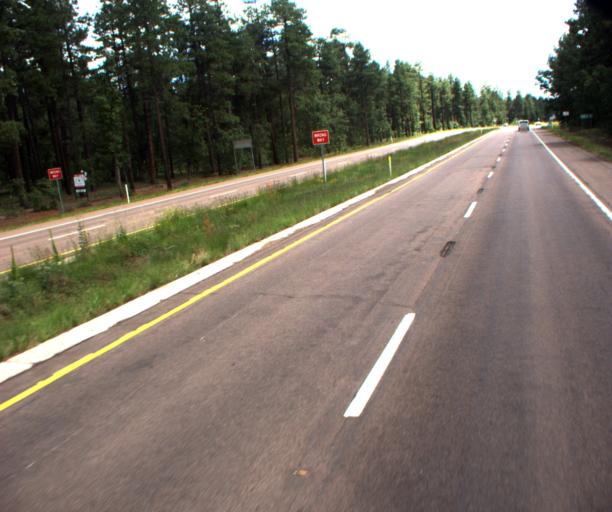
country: US
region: Arizona
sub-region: Navajo County
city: Pinetop-Lakeside
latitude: 34.1042
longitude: -109.9106
